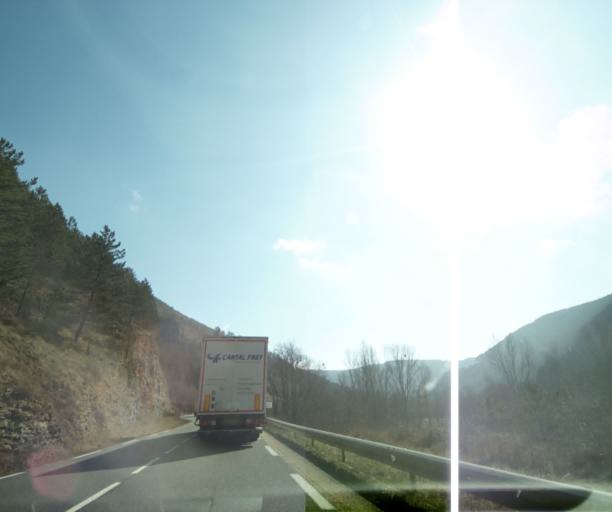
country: FR
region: Languedoc-Roussillon
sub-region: Departement de la Lozere
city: Chanac
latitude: 44.4933
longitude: 3.4153
